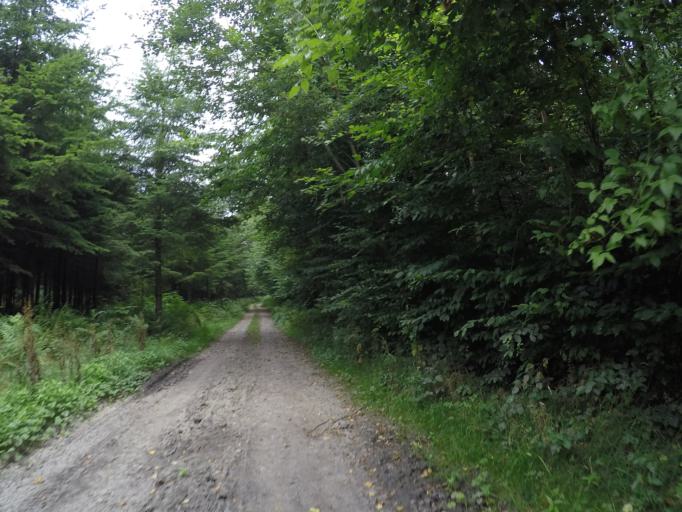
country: BE
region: Wallonia
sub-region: Province de Namur
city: Yvoir
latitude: 50.3326
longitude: 4.9474
